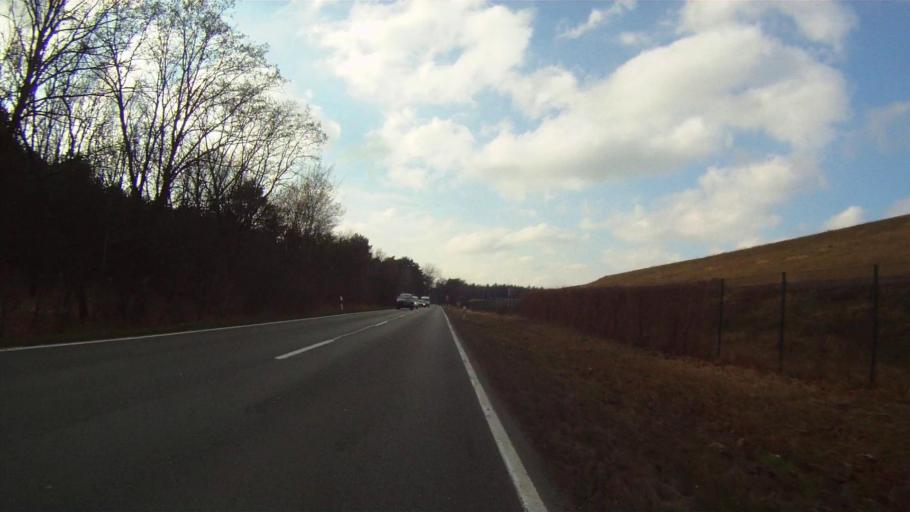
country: DE
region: Brandenburg
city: Erkner
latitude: 52.3838
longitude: 13.7263
